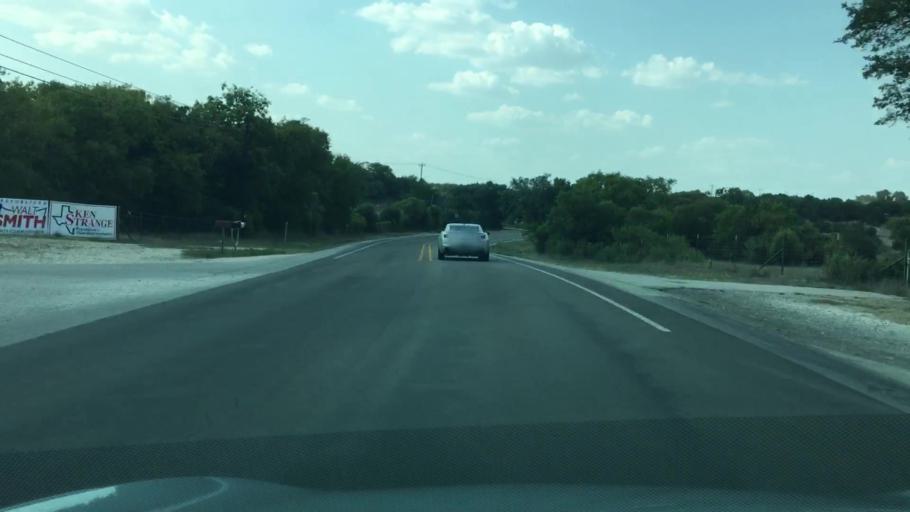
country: US
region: Texas
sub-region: Hays County
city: Dripping Springs
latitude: 30.1220
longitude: -98.0888
